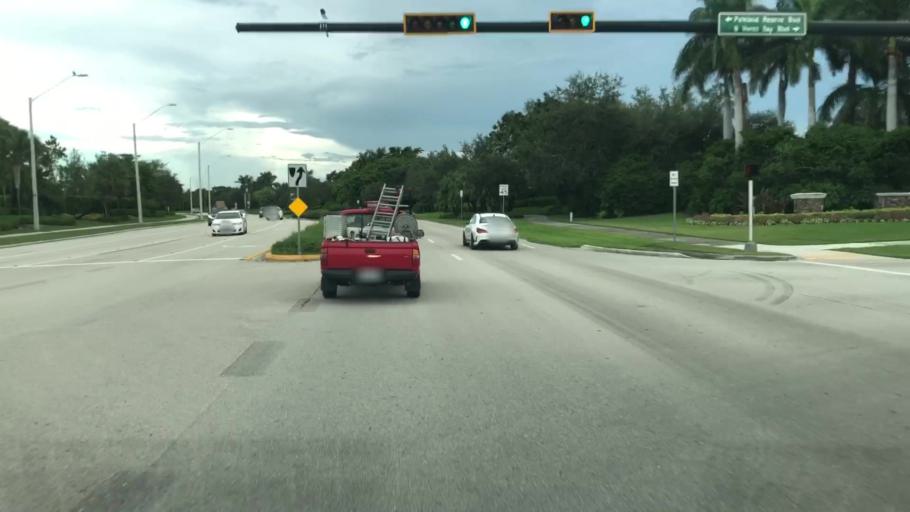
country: US
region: Florida
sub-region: Broward County
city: Parkland
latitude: 26.3242
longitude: -80.2775
